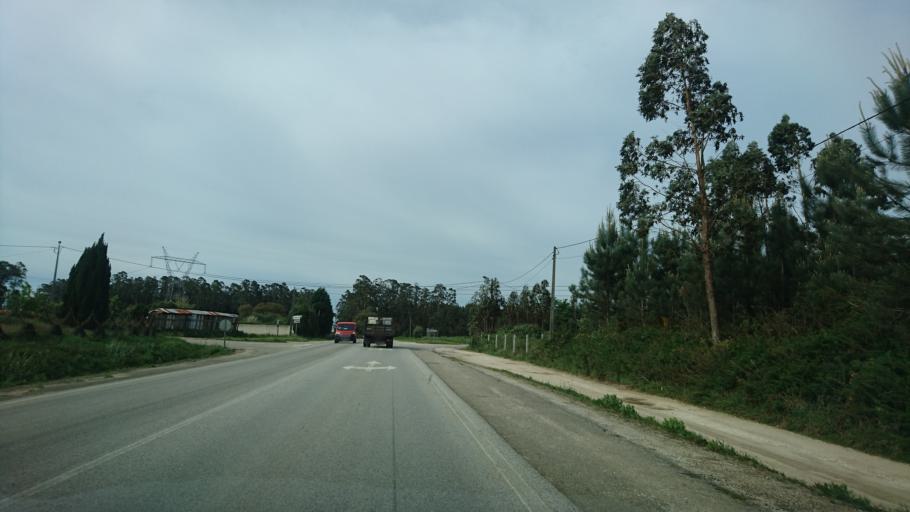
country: PT
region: Aveiro
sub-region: Albergaria-A-Velha
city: Albergaria-a-Velha
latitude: 40.6948
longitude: -8.5145
